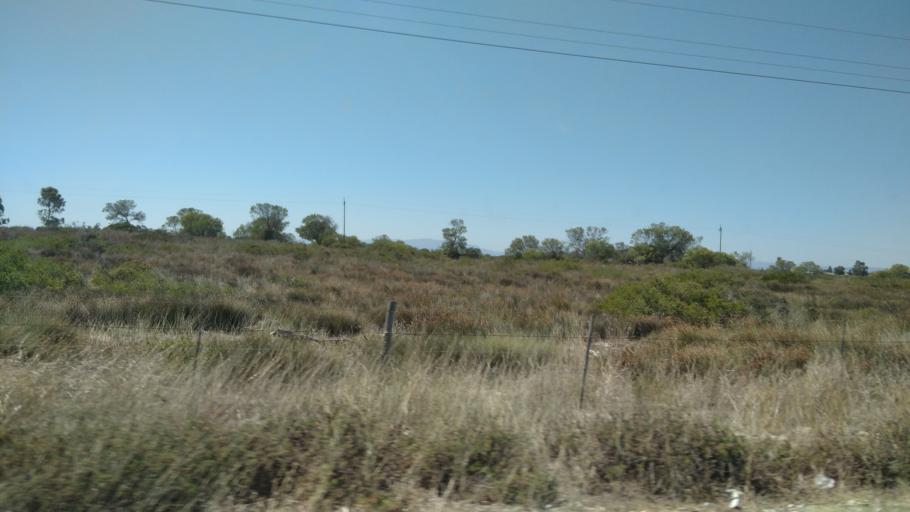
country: ZA
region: Western Cape
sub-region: West Coast District Municipality
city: Vredenburg
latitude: -33.0254
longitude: 18.2765
